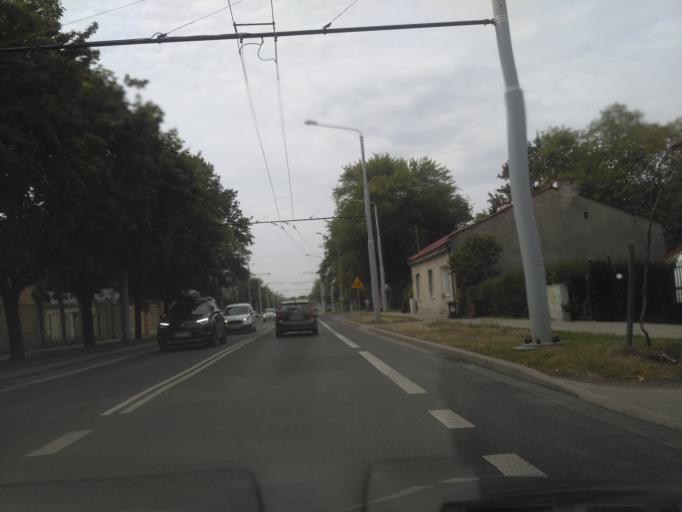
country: PL
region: Lublin Voivodeship
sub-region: Powiat lubelski
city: Lublin
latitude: 51.2247
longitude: 22.5490
